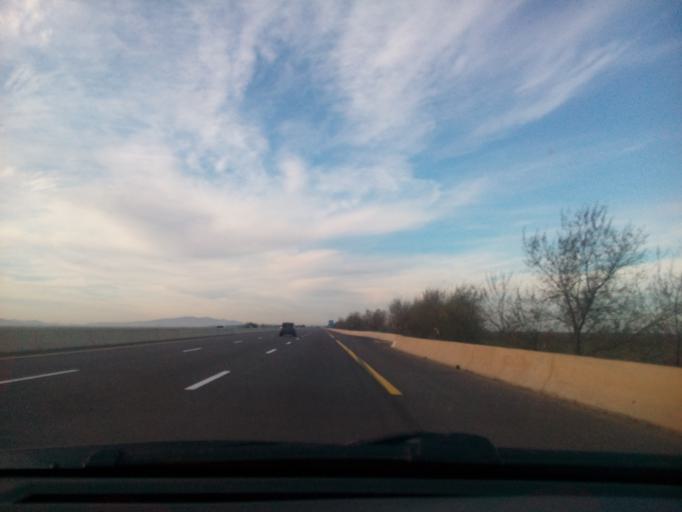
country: DZ
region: Mostaganem
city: Mostaganem
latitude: 35.6905
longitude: 0.1681
